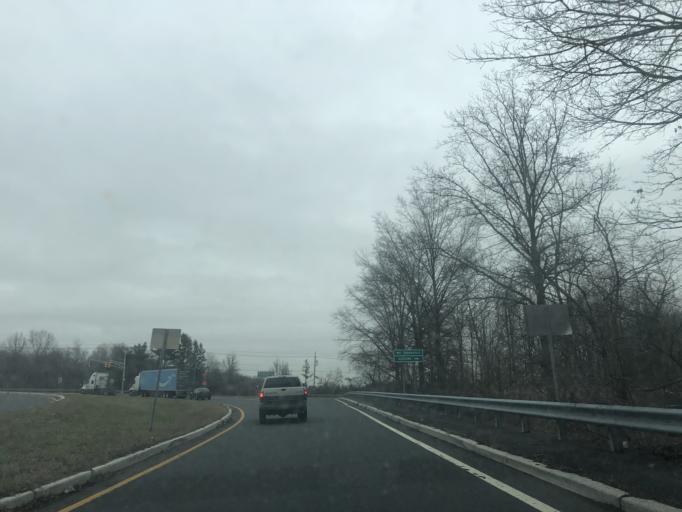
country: US
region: New Jersey
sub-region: Monmouth County
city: Allentown
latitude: 40.1907
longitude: -74.5937
